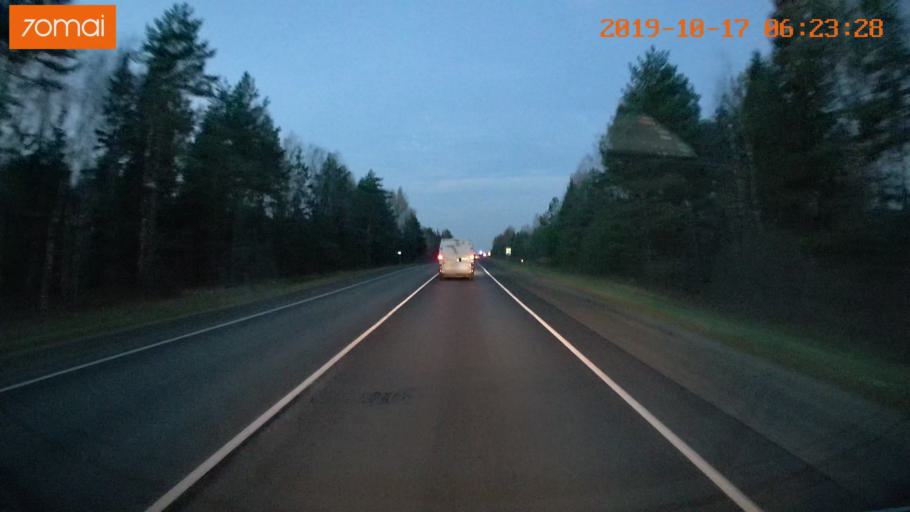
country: RU
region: Ivanovo
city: Lezhnevo
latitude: 56.7828
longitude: 40.8476
